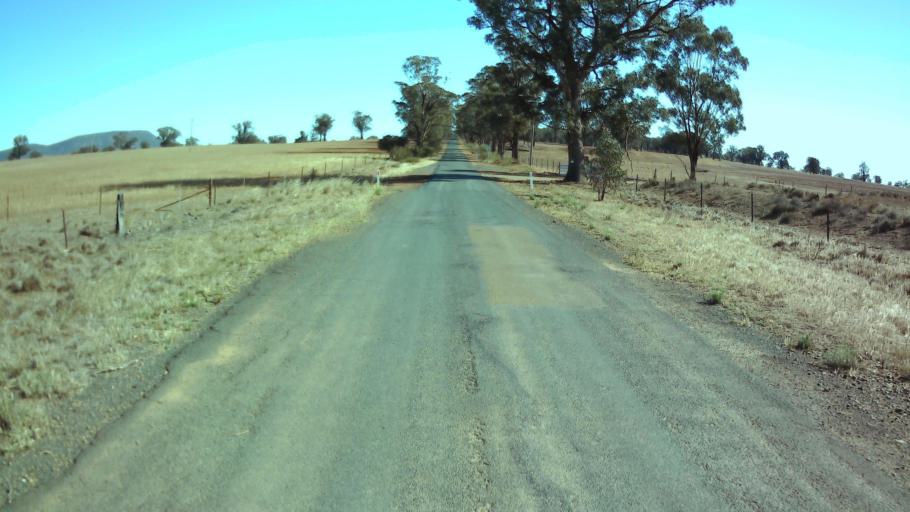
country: AU
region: New South Wales
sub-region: Weddin
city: Grenfell
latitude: -33.7917
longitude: 147.9573
